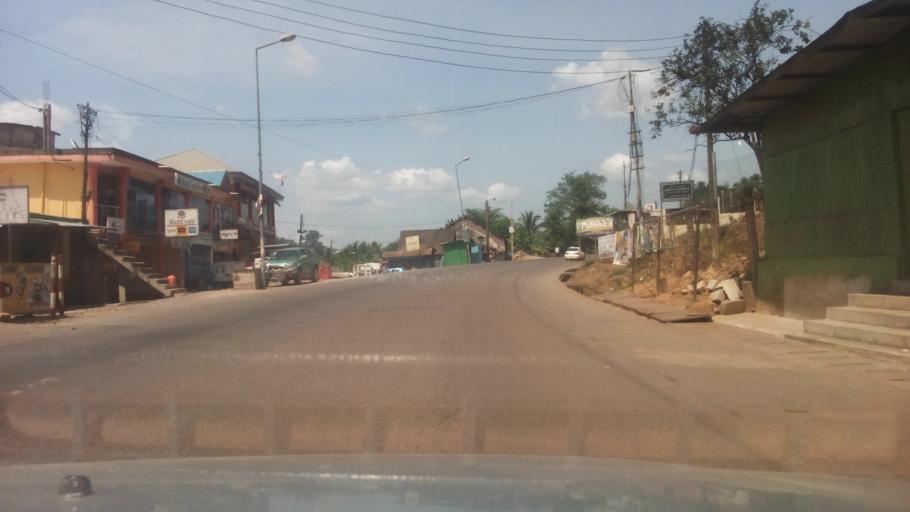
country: GH
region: Western
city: Tarkwa
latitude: 5.3081
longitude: -1.9942
